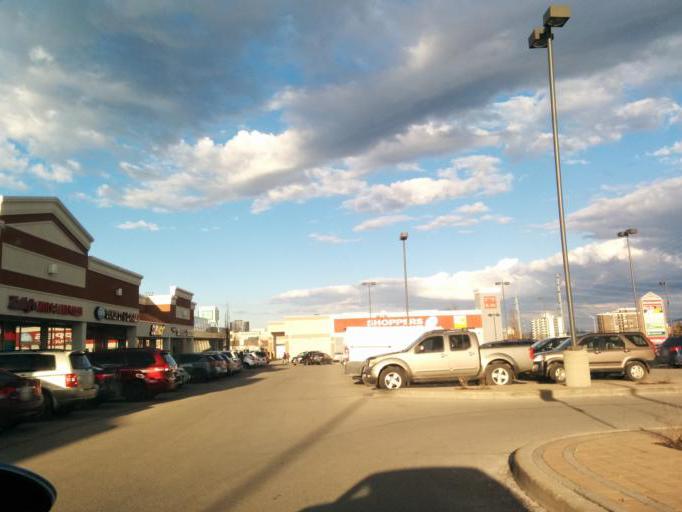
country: CA
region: Ontario
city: Mississauga
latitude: 43.5713
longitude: -79.6280
